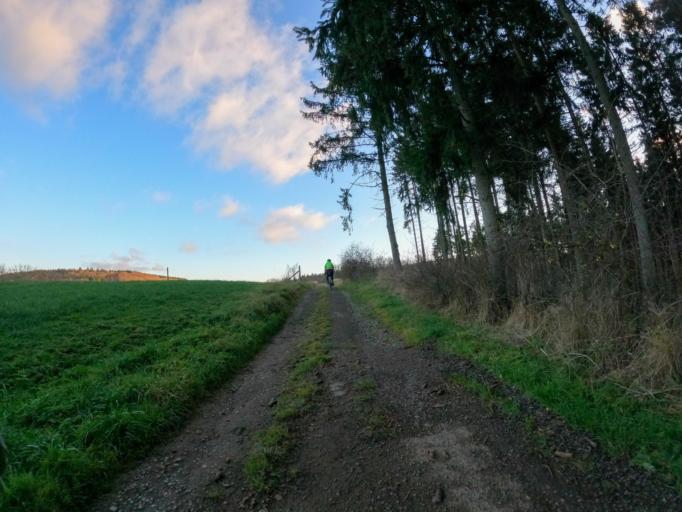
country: LU
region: Diekirch
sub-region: Canton de Wiltz
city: Bavigne
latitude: 49.9164
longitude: 5.8539
